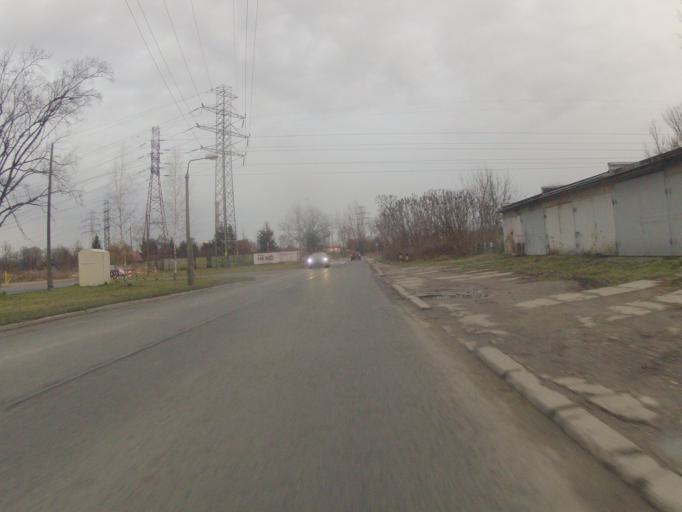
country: PL
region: Lesser Poland Voivodeship
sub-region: Krakow
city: Krakow
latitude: 50.0511
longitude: 20.0039
